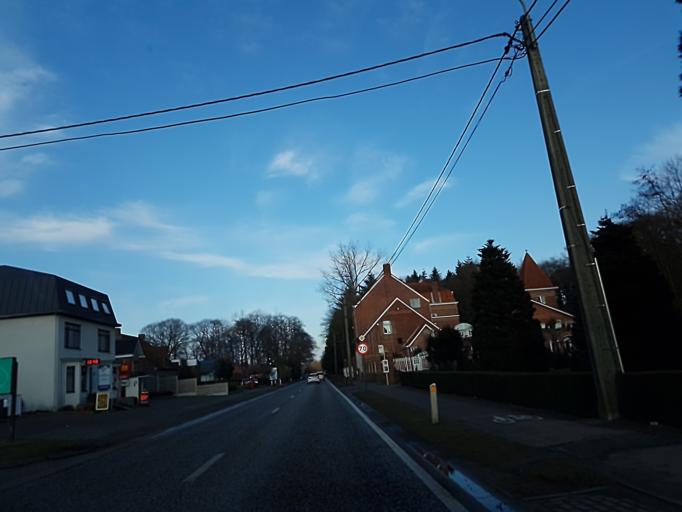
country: BE
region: Flanders
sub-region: Provincie Antwerpen
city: Oud-Turnhout
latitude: 51.3468
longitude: 4.9783
